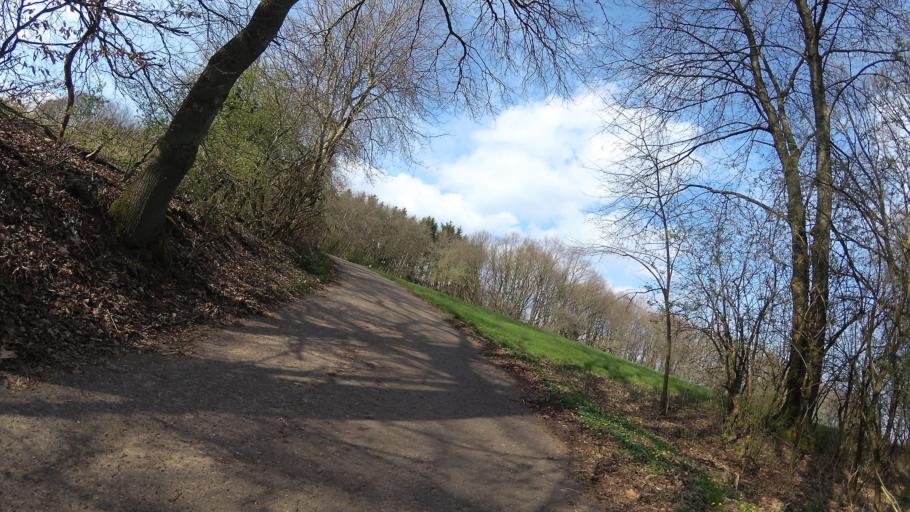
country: DE
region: Saarland
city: Ottweiler
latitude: 49.3949
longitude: 7.1438
